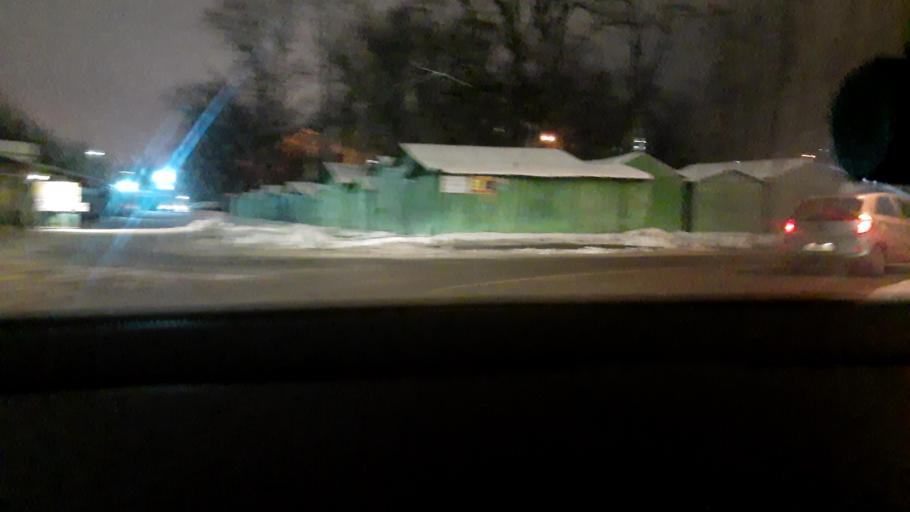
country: RU
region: Moscow
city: Vatutino
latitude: 55.8644
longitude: 37.6900
